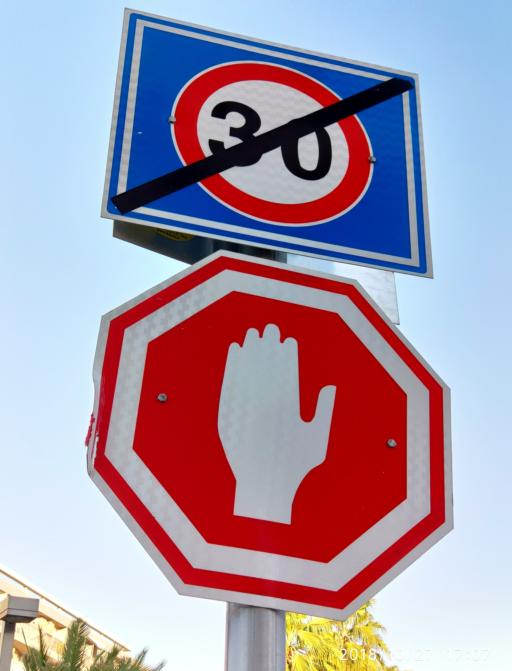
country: IL
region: Tel Aviv
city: Yafo
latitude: 32.0549
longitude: 34.7577
